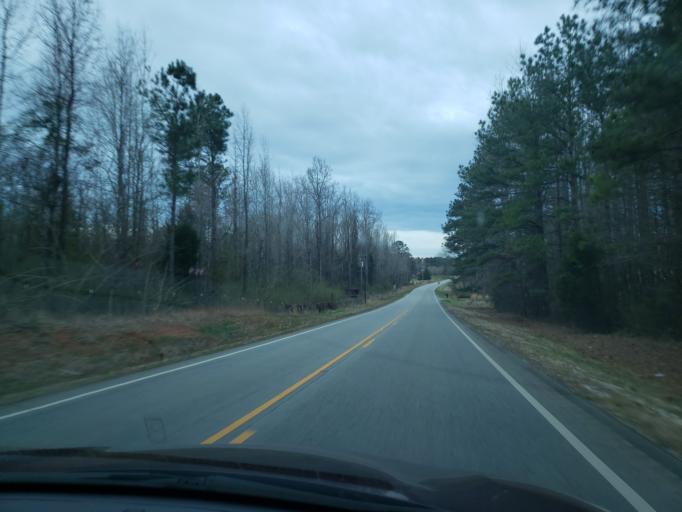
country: US
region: Alabama
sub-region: Chambers County
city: Lafayette
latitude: 32.9633
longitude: -85.4031
